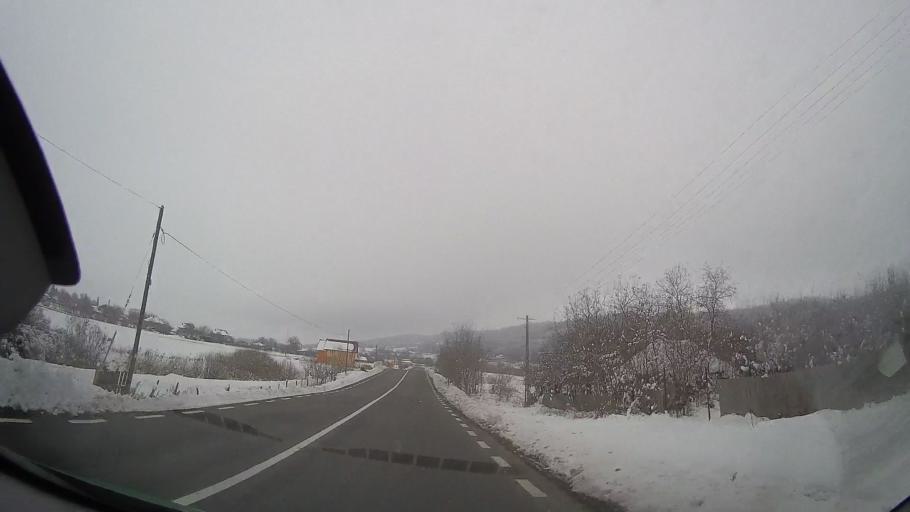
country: RO
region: Neamt
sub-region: Comuna Bozieni
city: Bozieni
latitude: 46.8551
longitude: 27.1739
